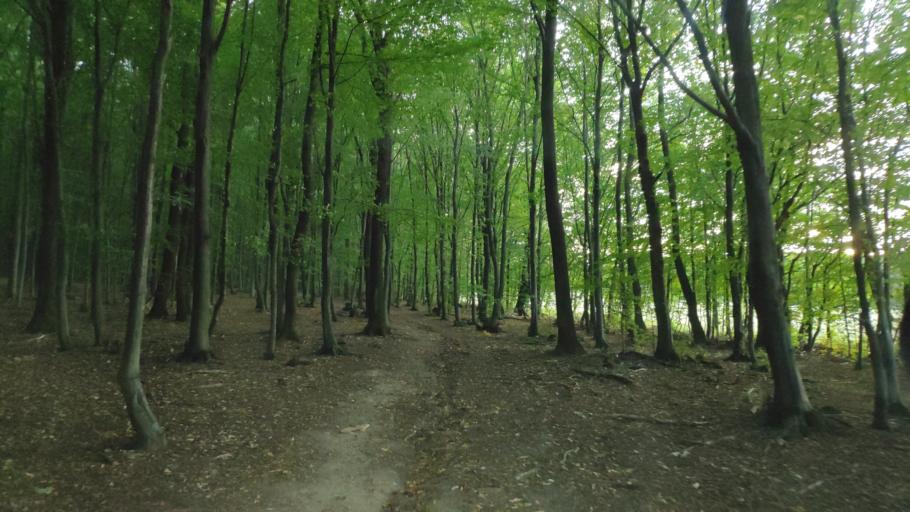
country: SK
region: Kosicky
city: Kosice
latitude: 48.7027
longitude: 21.1923
